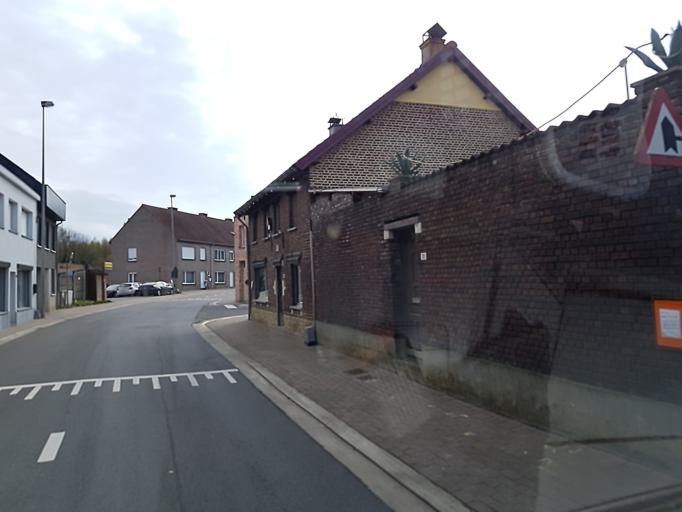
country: BE
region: Flanders
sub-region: Provincie Vlaams-Brabant
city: Scherpenheuvel-Zichem
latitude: 50.9988
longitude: 4.9895
